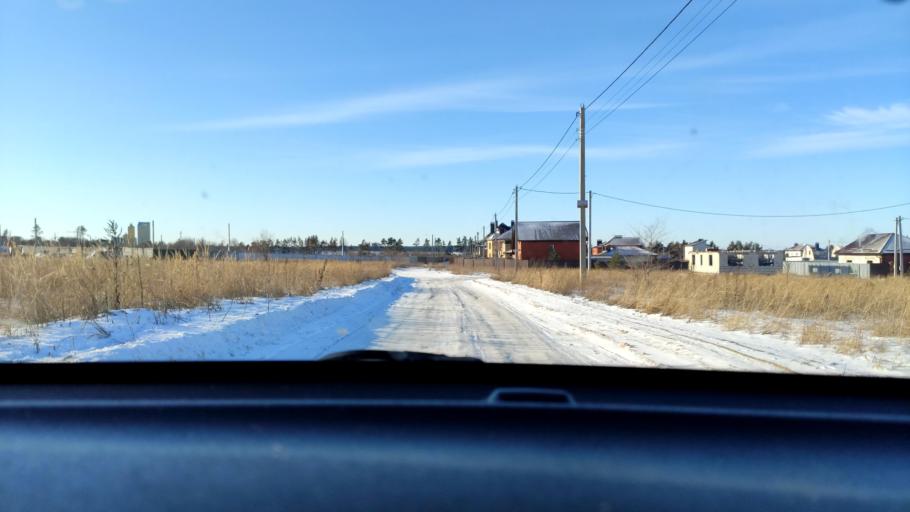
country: RU
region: Voronezj
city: Podgornoye
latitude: 51.7230
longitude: 39.1356
